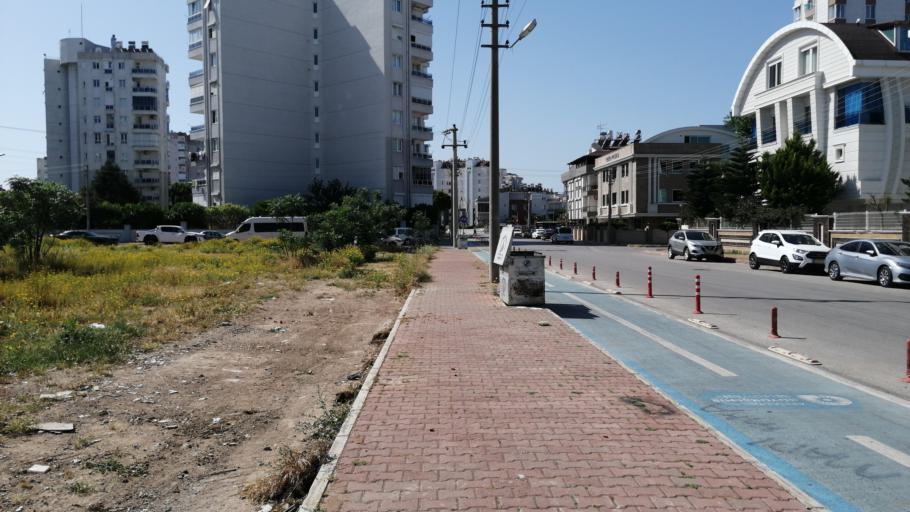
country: TR
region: Antalya
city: Antalya
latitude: 36.8580
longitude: 30.7834
